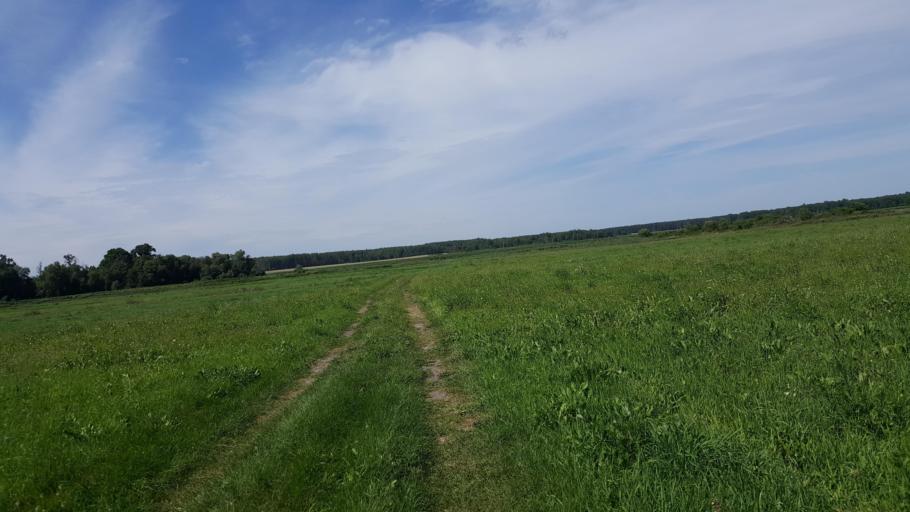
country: BY
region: Brest
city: Zhabinka
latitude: 52.4640
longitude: 24.1058
